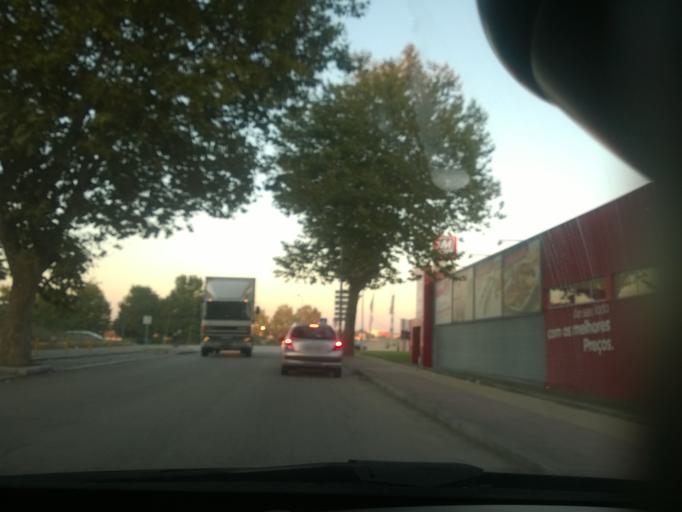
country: PT
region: Porto
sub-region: Matosinhos
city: Santa Cruz do Bispo
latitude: 41.2235
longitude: -8.6965
